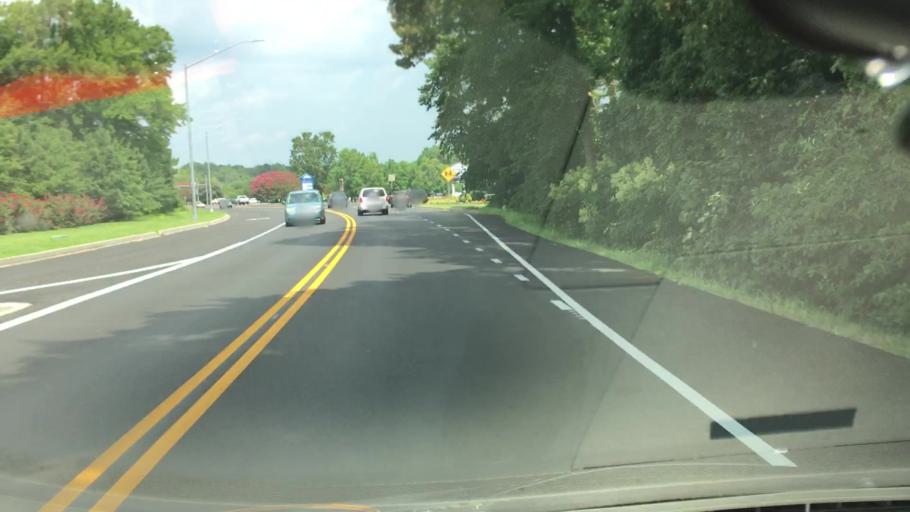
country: US
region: Maryland
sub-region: Worcester County
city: Ocean Pines
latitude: 38.3736
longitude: -75.1632
